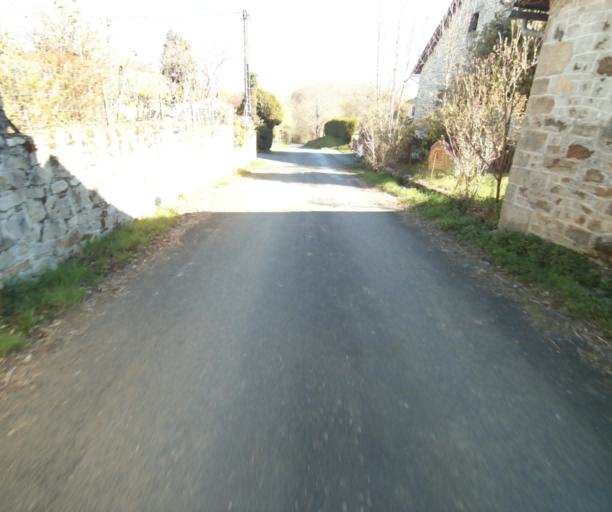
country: FR
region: Limousin
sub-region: Departement de la Correze
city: Chamboulive
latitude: 45.4122
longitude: 1.6986
